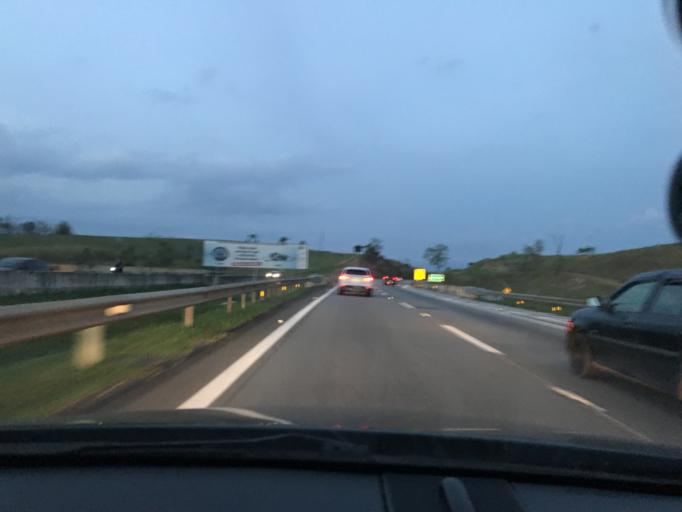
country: BR
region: Sao Paulo
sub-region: Mogi das Cruzes
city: Mogi das Cruzes
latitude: -23.4191
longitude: -46.2037
